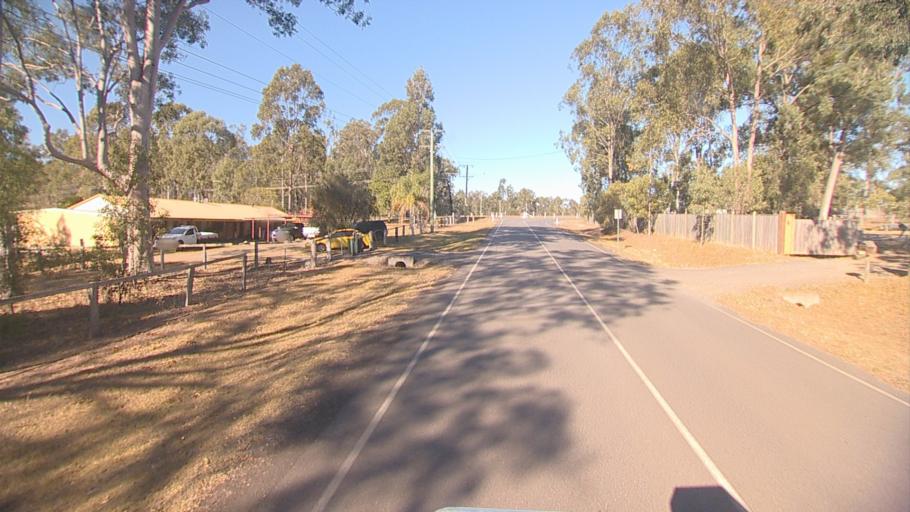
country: AU
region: Queensland
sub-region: Logan
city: North Maclean
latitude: -27.8208
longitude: 152.9876
